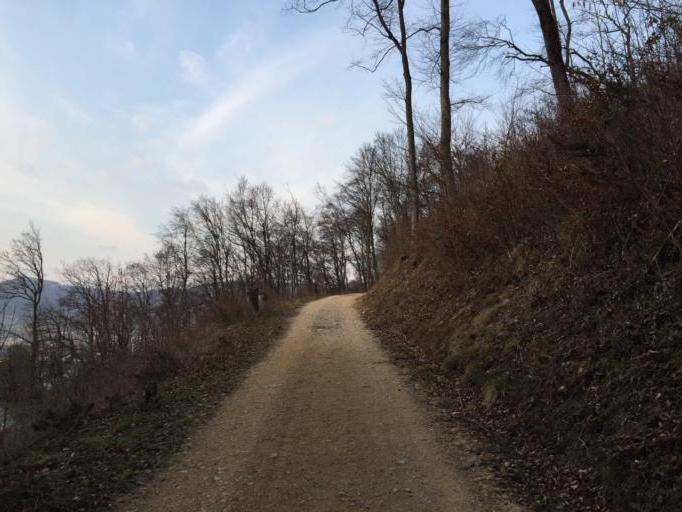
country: CH
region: Basel-Landschaft
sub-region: Bezirk Sissach
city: Sissach
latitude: 47.4570
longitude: 7.8141
